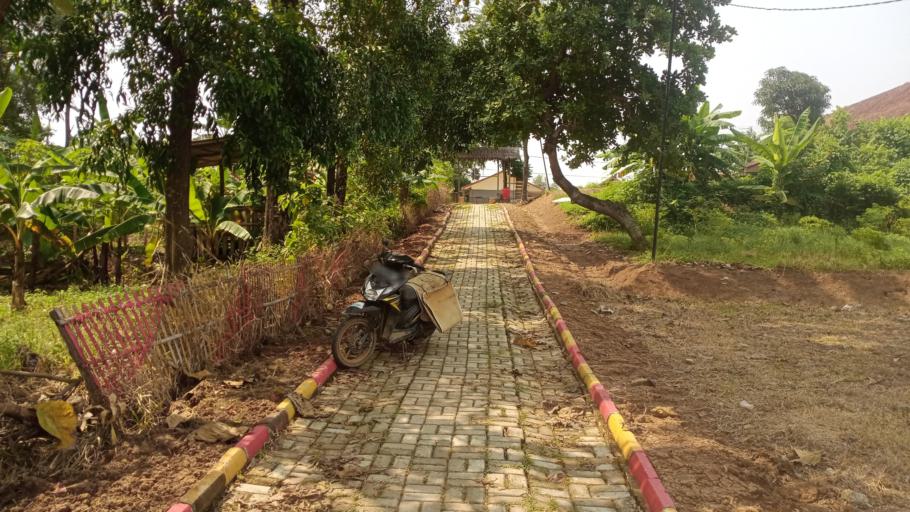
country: ID
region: West Java
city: Cikarang
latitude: -6.3430
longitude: 107.1822
